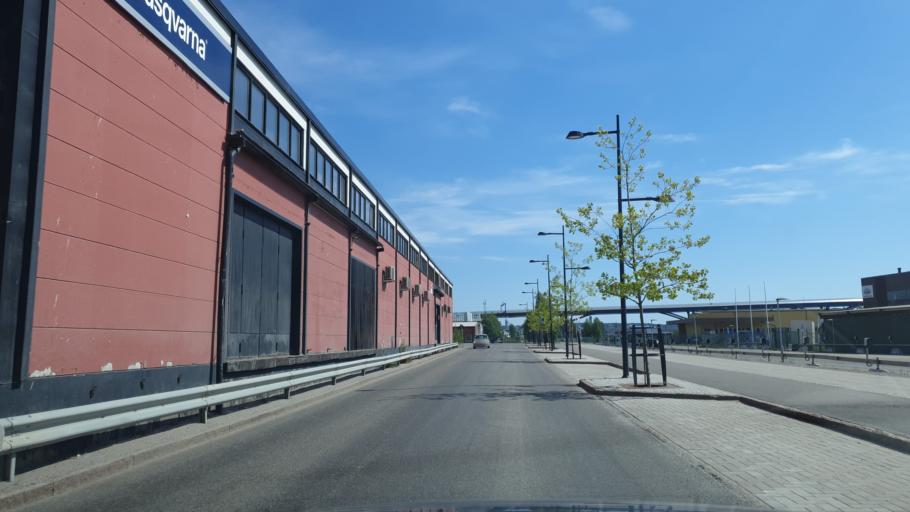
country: SE
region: Vaesternorrland
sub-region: Sundsvalls Kommun
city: Sundsvall
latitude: 62.3944
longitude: 17.3261
